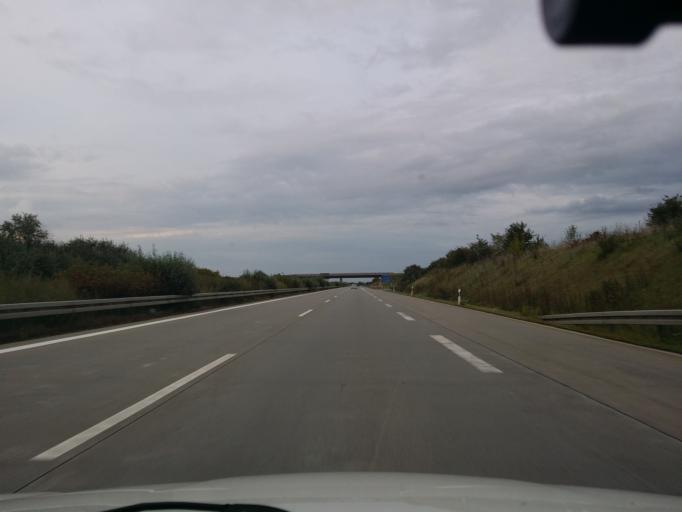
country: DE
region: Saxony-Anhalt
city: Lutzen
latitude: 51.2378
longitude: 12.1337
